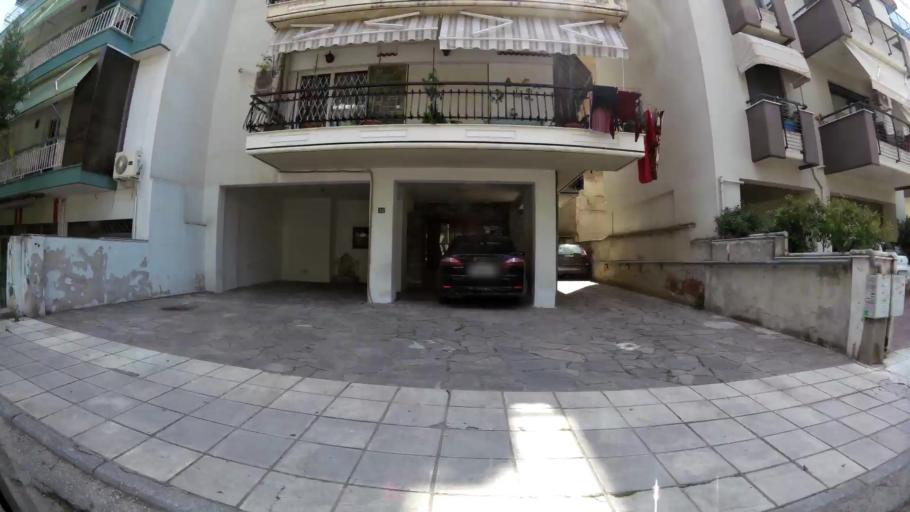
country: GR
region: Central Macedonia
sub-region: Nomos Thessalonikis
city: Triandria
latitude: 40.6185
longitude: 22.9738
